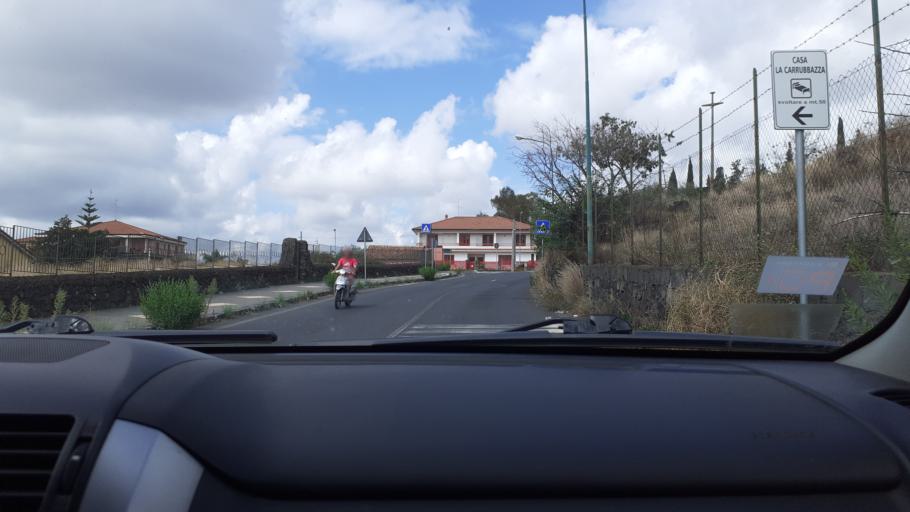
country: IT
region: Sicily
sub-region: Catania
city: Carrubazza-Motta
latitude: 37.5581
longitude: 15.1071
